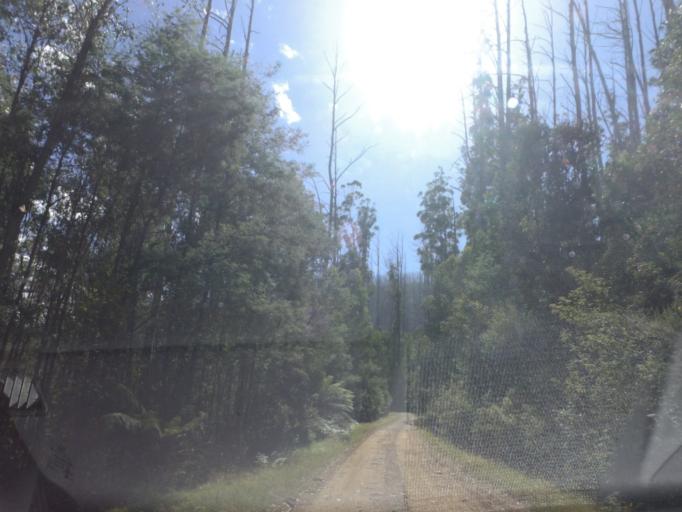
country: AU
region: Victoria
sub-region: Yarra Ranges
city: Millgrove
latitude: -37.5027
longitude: 145.8472
